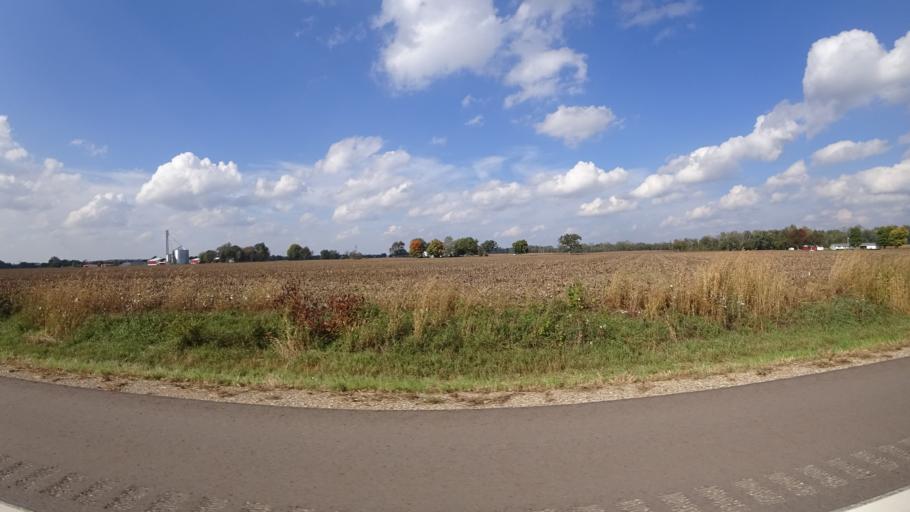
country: US
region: Michigan
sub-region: Branch County
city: Union City
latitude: 42.0702
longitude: -85.1508
